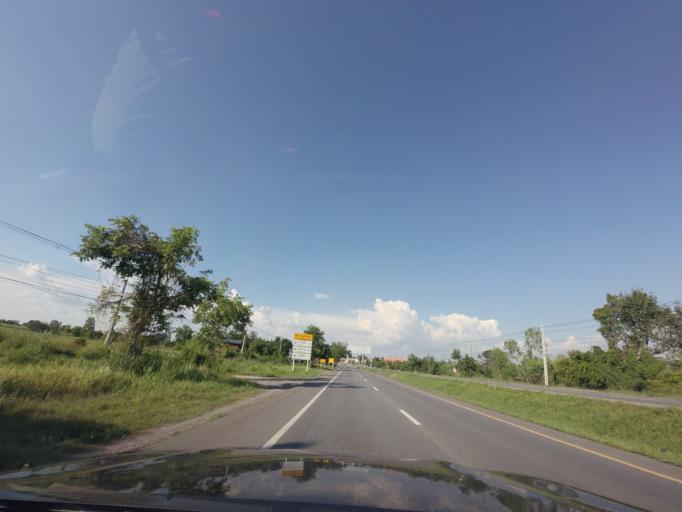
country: TH
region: Khon Kaen
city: Non Sila
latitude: 15.9588
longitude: 102.6881
